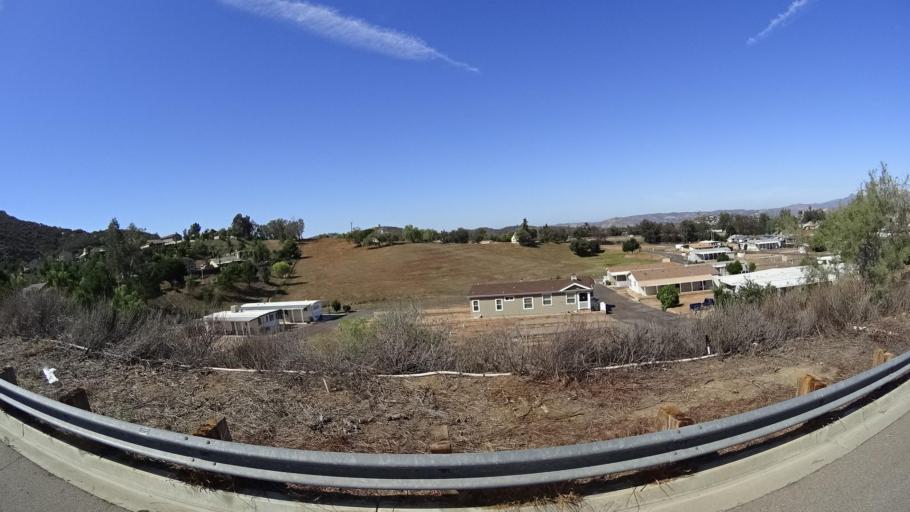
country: US
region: California
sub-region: San Diego County
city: Granite Hills
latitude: 32.8291
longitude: -116.8937
